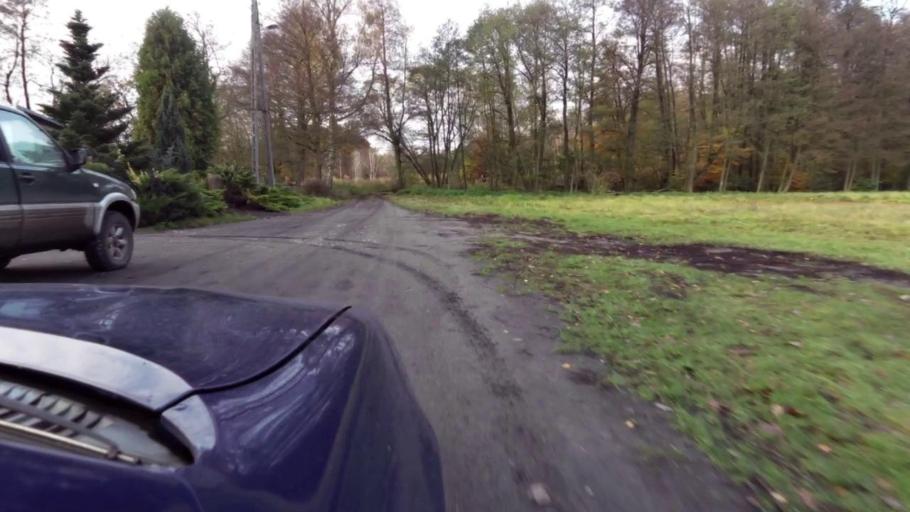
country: PL
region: West Pomeranian Voivodeship
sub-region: Powiat goleniowski
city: Goleniow
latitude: 53.6087
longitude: 14.7532
